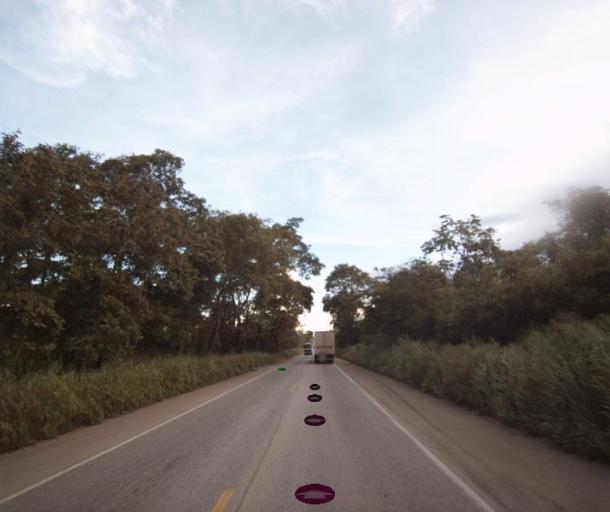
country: BR
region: Goias
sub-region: Uruacu
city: Uruacu
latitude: -14.2423
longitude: -49.1373
